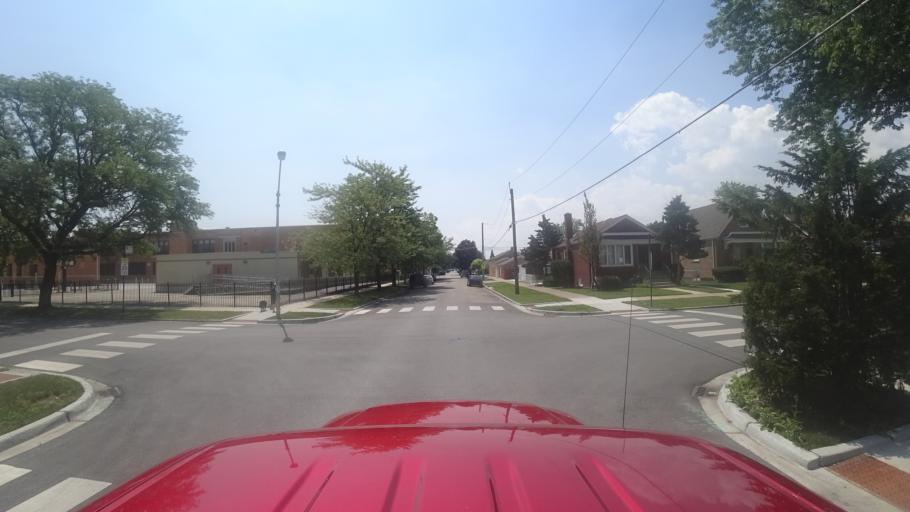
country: US
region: Illinois
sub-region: Cook County
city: Hometown
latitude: 41.7888
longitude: -87.7206
